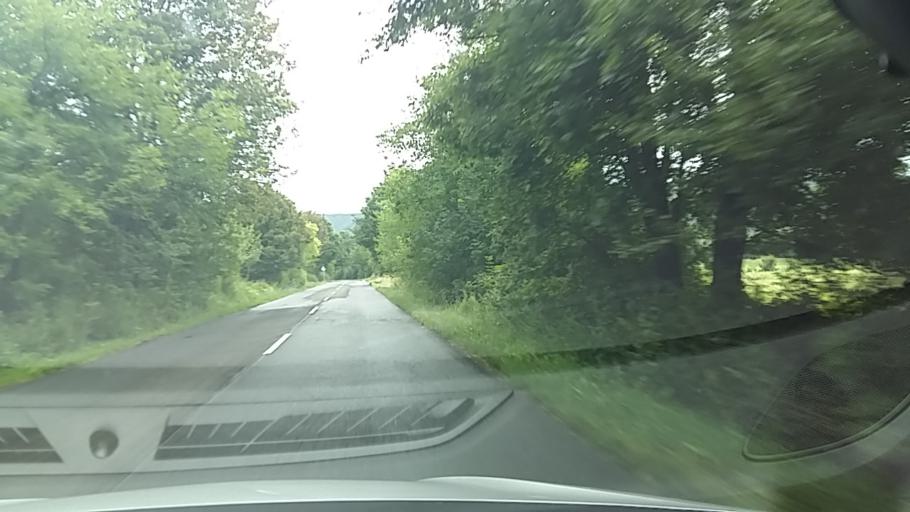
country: HU
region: Komarom-Esztergom
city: Esztergom
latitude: 47.8699
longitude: 18.7892
